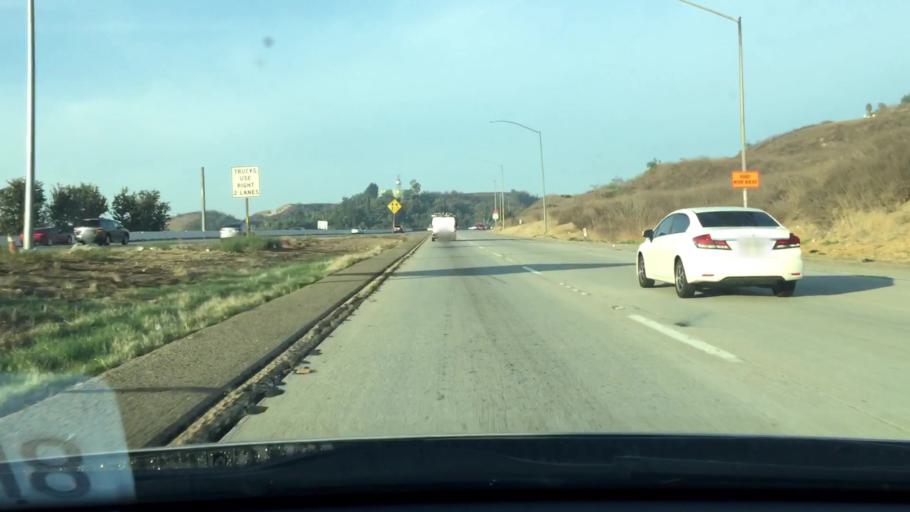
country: US
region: California
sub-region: Los Angeles County
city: Diamond Bar
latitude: 34.0641
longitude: -117.8160
